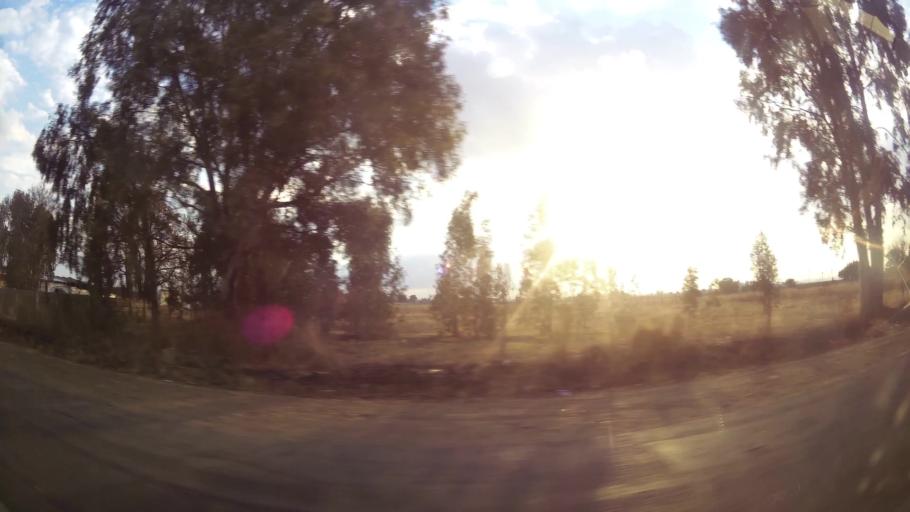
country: ZA
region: Gauteng
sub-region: Sedibeng District Municipality
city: Vanderbijlpark
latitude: -26.6328
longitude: 27.8083
